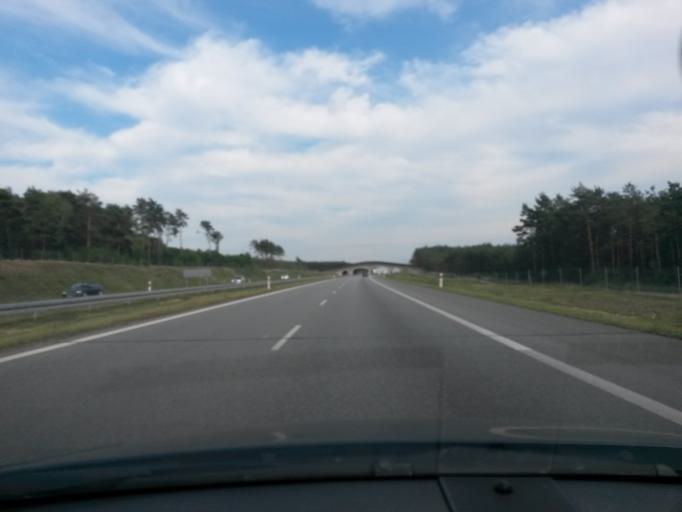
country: PL
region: Greater Poland Voivodeship
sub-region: Powiat turecki
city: Tuliszkow
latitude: 52.1466
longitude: 18.3124
